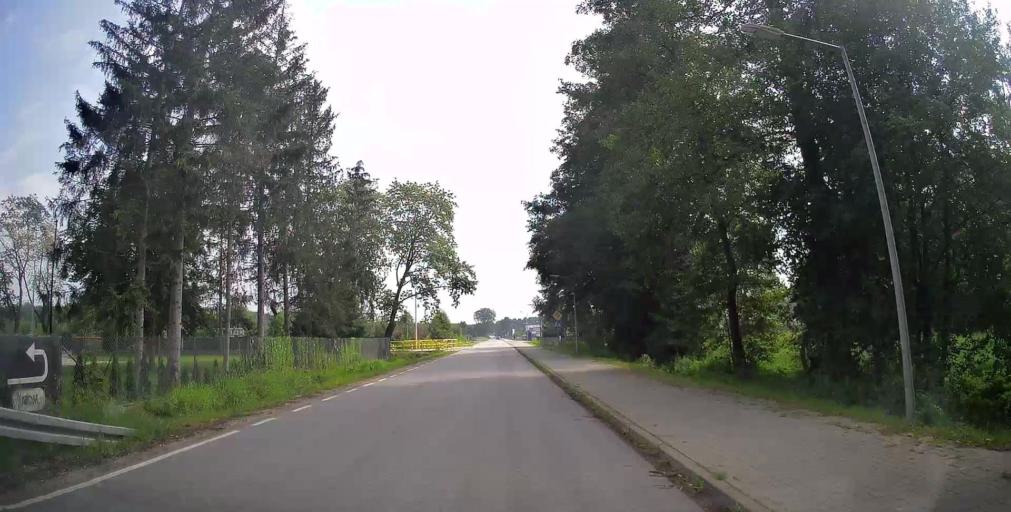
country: PL
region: Masovian Voivodeship
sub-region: Powiat bialobrzeski
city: Sucha
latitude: 51.6173
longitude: 20.9566
